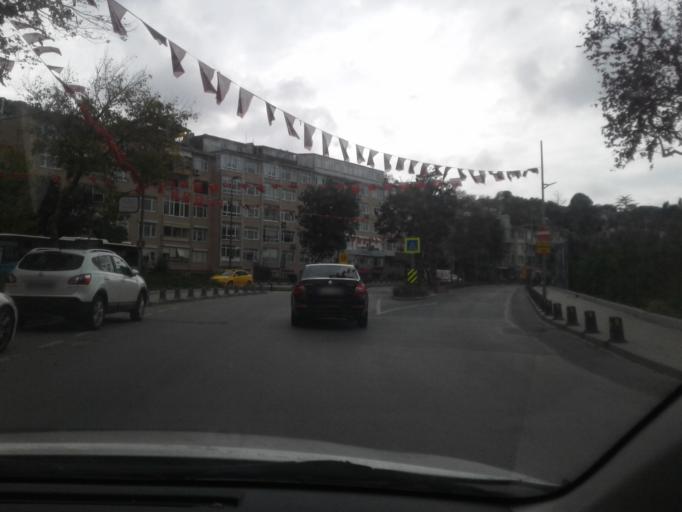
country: TR
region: Istanbul
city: UEskuedar
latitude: 41.0486
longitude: 29.0543
